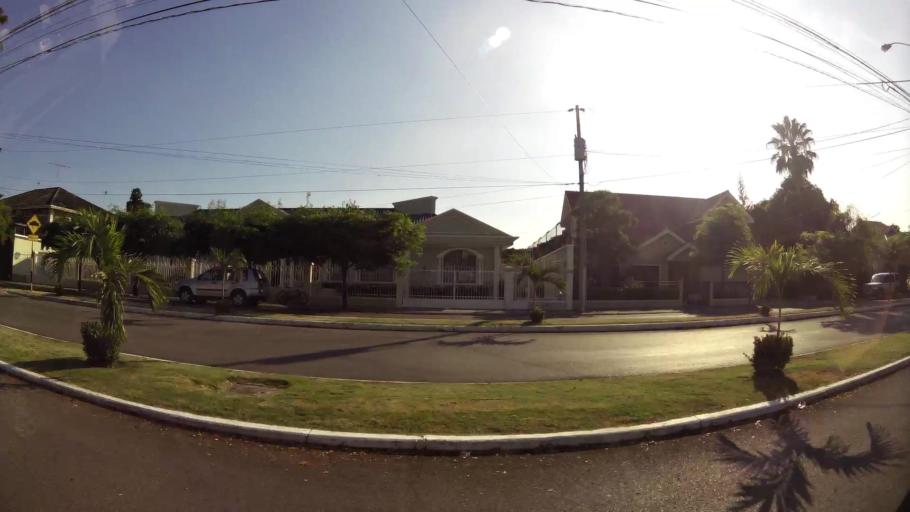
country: EC
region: Guayas
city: Santa Lucia
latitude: -2.1904
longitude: -79.9679
